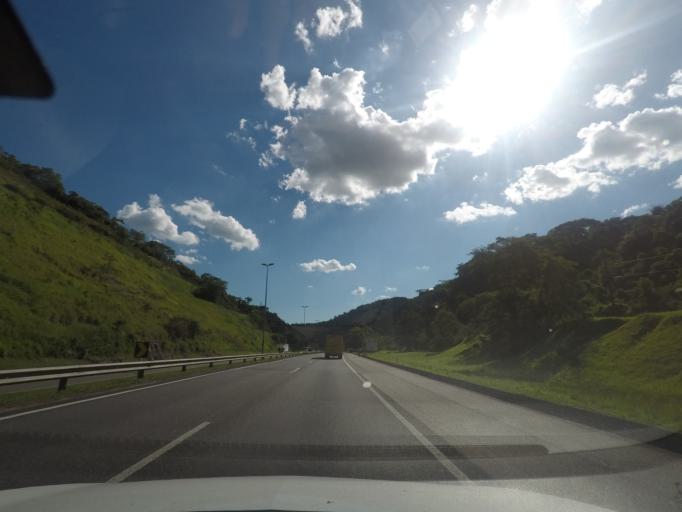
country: BR
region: Rio de Janeiro
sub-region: Guapimirim
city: Guapimirim
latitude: -22.5678
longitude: -43.0025
